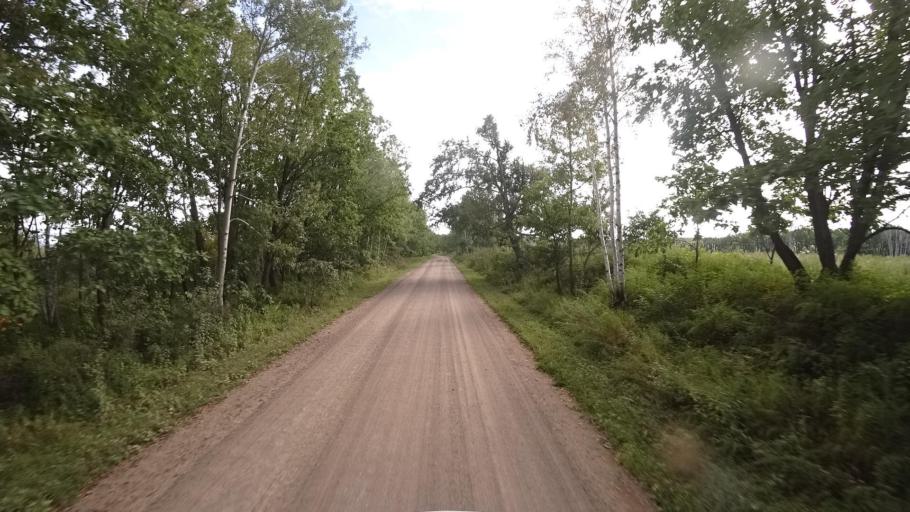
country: RU
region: Primorskiy
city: Dostoyevka
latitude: 44.3652
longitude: 133.5204
